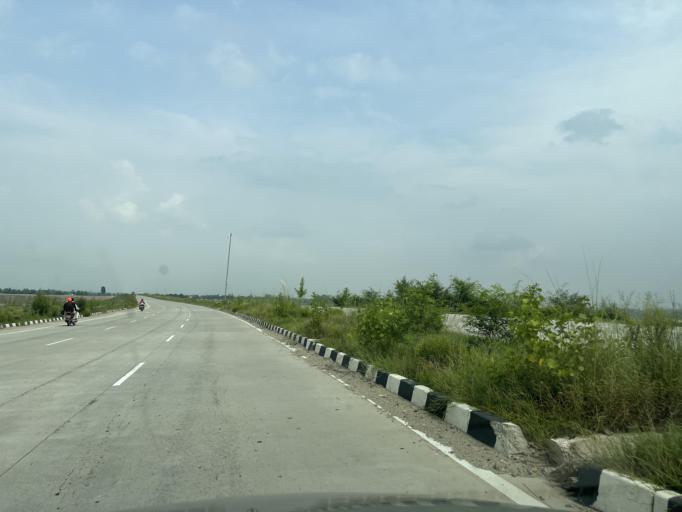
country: IN
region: Uttarakhand
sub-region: Udham Singh Nagar
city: Bazpur
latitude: 29.1466
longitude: 79.0319
